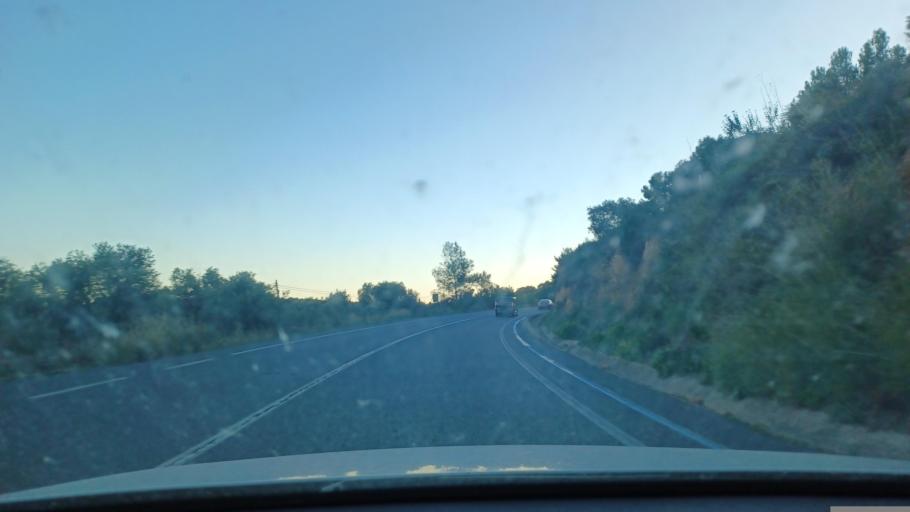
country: ES
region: Catalonia
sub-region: Provincia de Tarragona
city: Alcover
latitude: 41.3010
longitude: 1.1970
